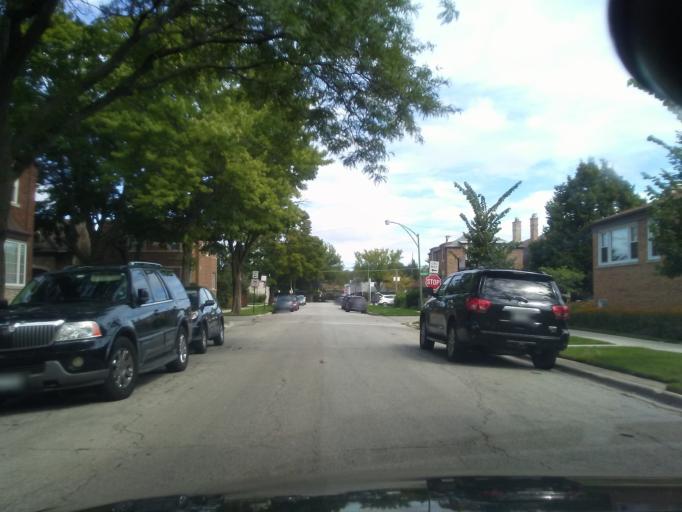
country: US
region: Illinois
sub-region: Cook County
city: Lincolnwood
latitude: 42.0107
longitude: -87.7021
